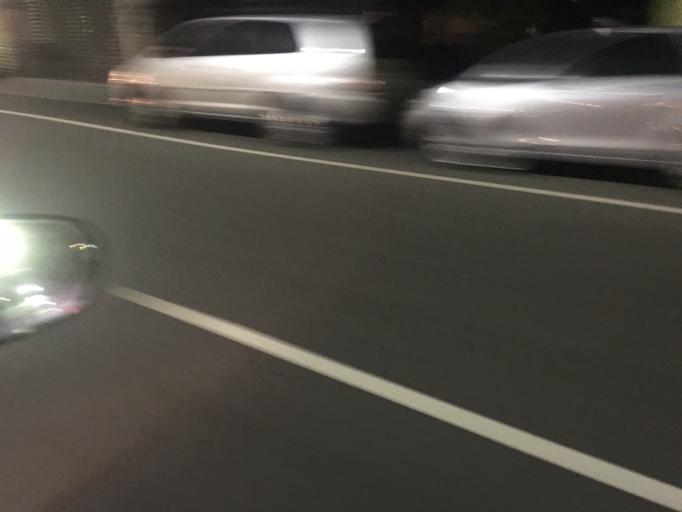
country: TW
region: Taiwan
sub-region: Hsinchu
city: Hsinchu
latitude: 24.8141
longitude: 120.9704
